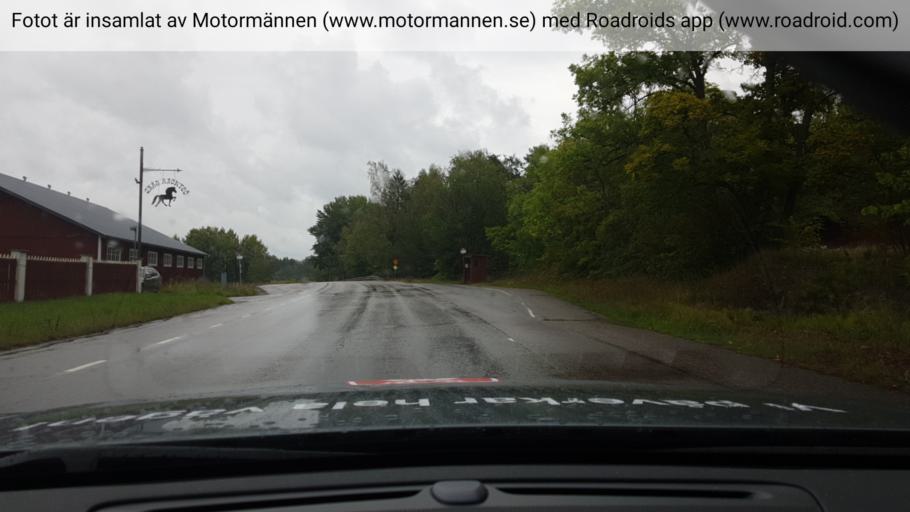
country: SE
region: Stockholm
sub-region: Haninge Kommun
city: Jordbro
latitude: 59.0598
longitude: 18.0453
